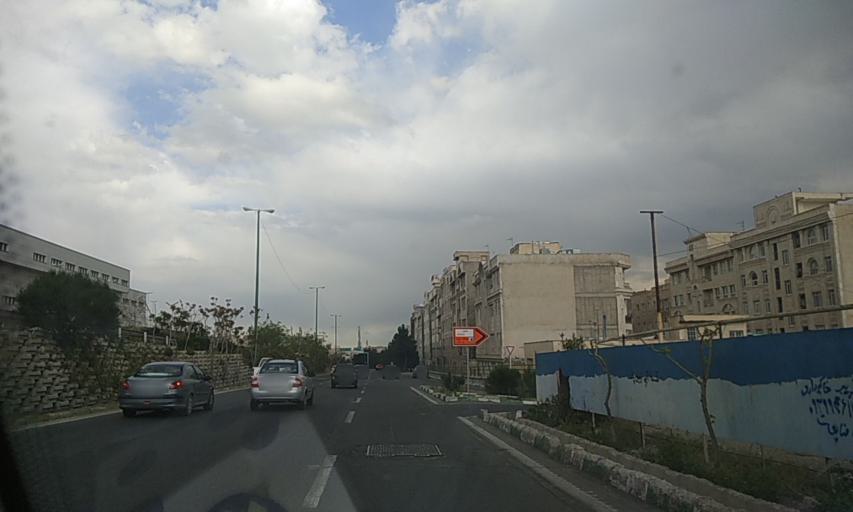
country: IR
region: Tehran
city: Tajrish
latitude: 35.7782
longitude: 51.3150
